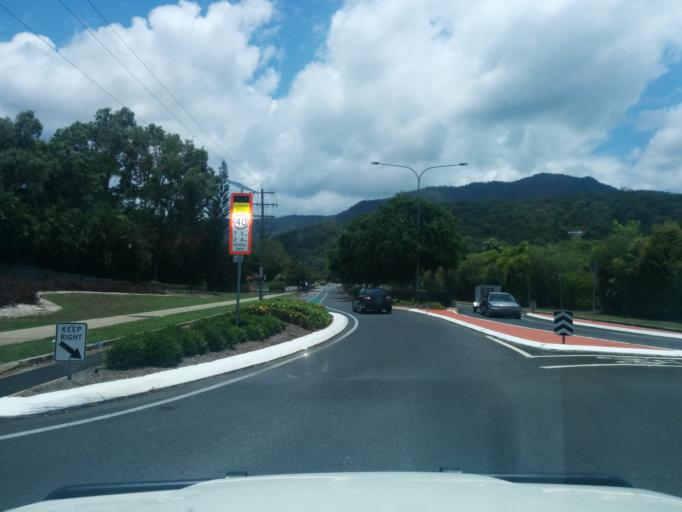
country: AU
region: Queensland
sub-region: Cairns
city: Trinity Beach
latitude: -16.8089
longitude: 145.6969
